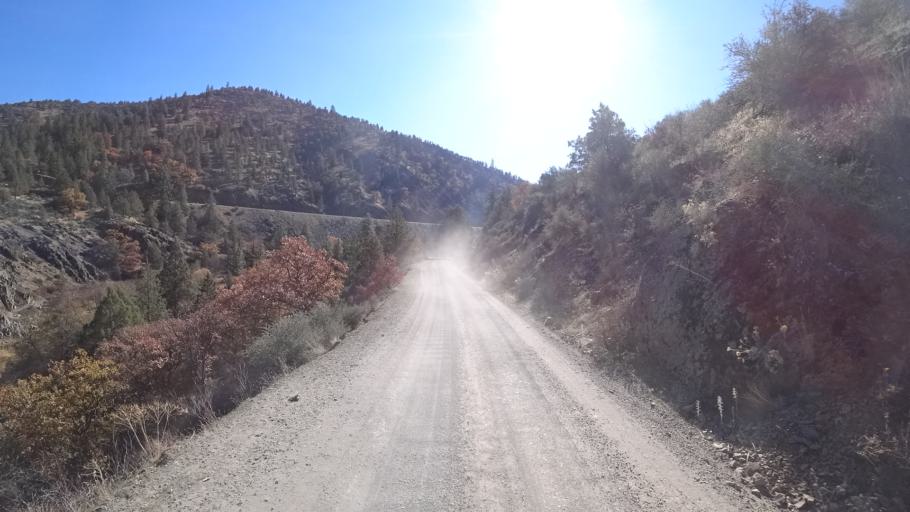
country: US
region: California
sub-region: Siskiyou County
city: Yreka
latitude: 41.7987
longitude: -122.6055
